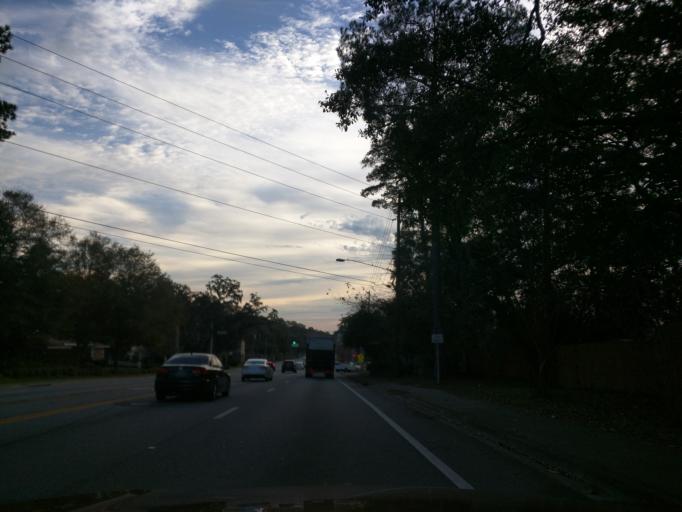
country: US
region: Florida
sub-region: Leon County
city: Tallahassee
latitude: 30.4636
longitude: -84.2930
